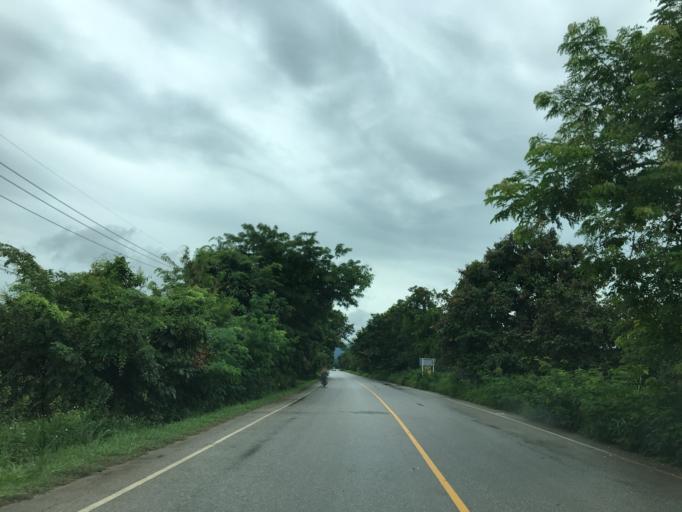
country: TH
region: Chiang Rai
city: Pa Daet
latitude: 19.4977
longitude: 99.9746
